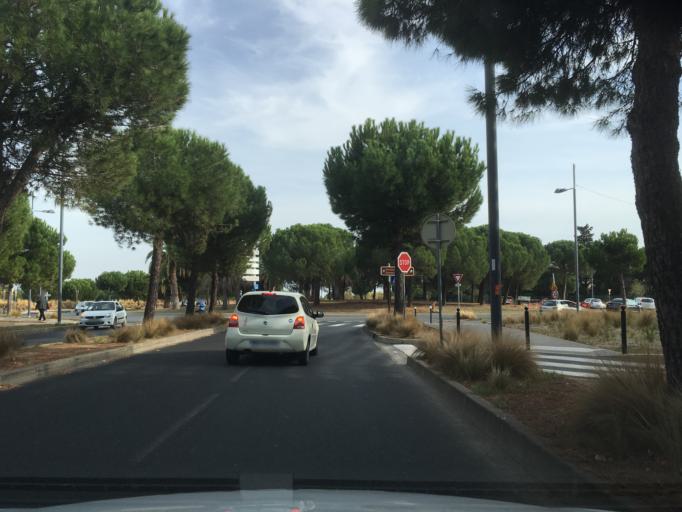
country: FR
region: Languedoc-Roussillon
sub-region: Departement de l'Herault
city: Castelnau-le-Lez
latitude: 43.6021
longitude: 3.9156
